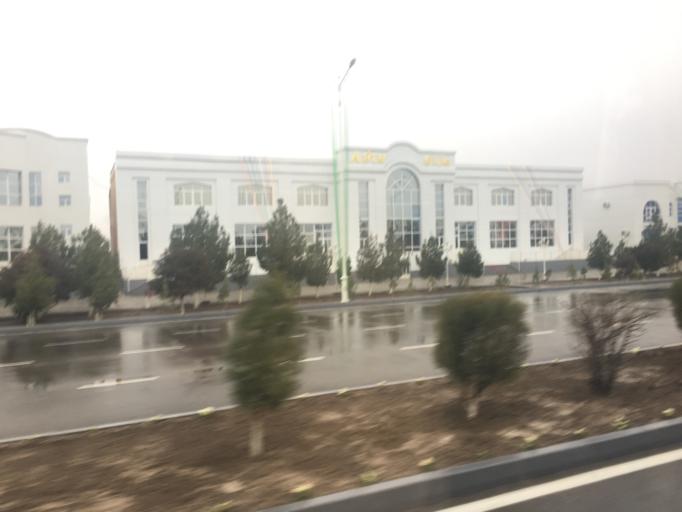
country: TM
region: Lebap
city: Turkmenabat
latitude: 39.0690
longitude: 63.5870
